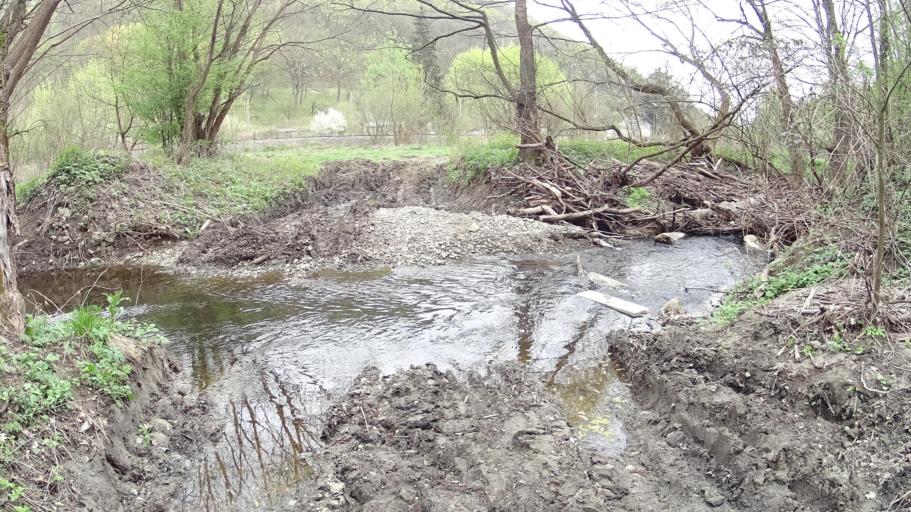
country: HU
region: Pest
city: Kismaros
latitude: 47.8745
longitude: 19.0289
